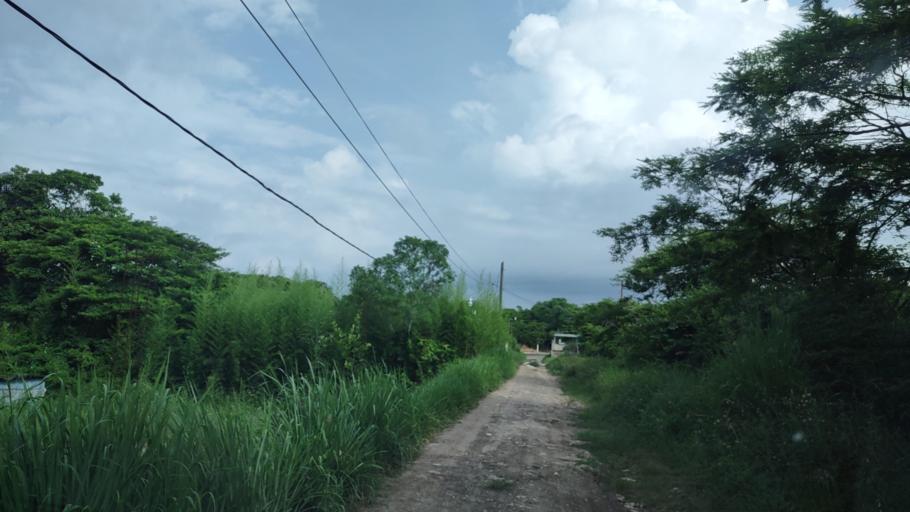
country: MX
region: Veracruz
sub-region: Coatepec
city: Bella Esperanza
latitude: 19.4483
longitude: -96.8274
